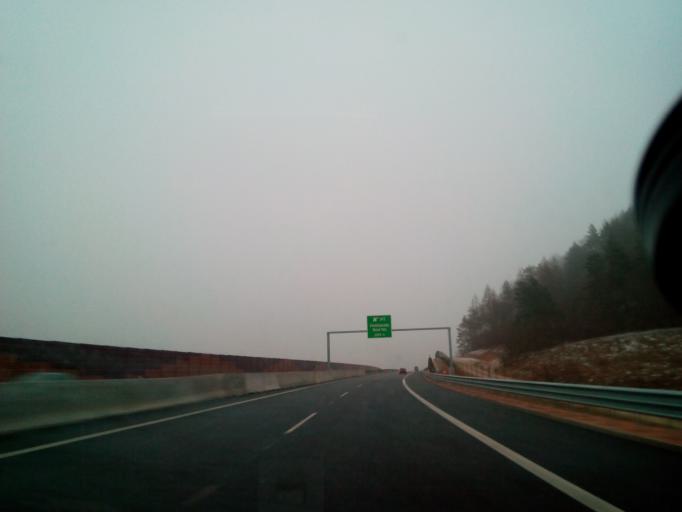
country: SK
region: Presovsky
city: Sabinov
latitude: 48.9999
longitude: 21.0786
